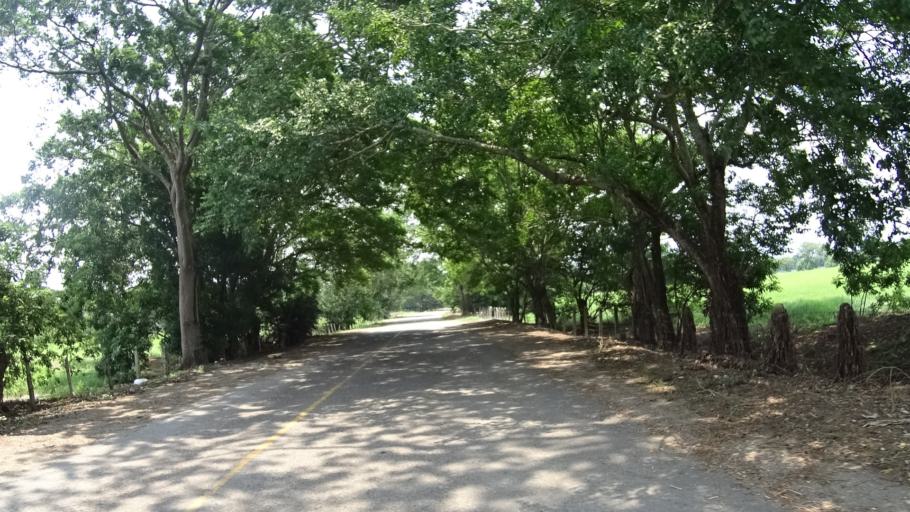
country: CO
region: Cundinamarca
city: Puerto Salgar
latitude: 5.4925
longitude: -74.6805
